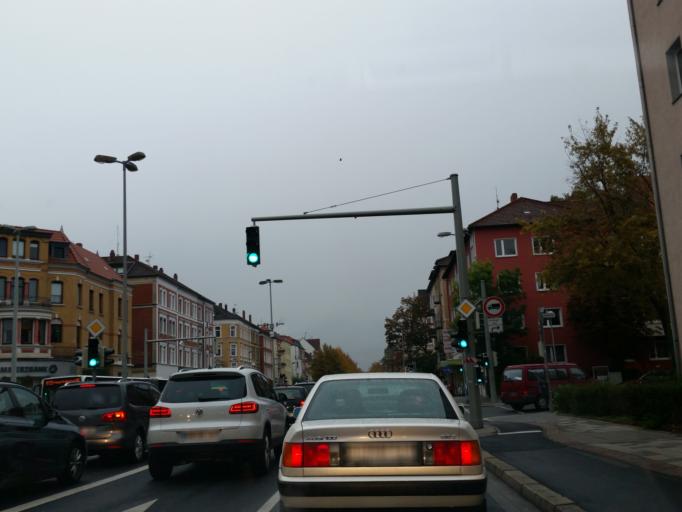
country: DE
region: Lower Saxony
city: Braunschweig
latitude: 52.2682
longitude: 10.5397
